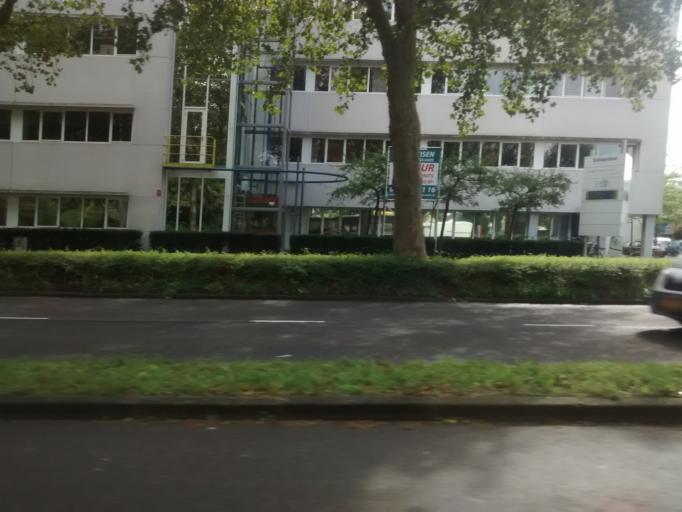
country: NL
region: Utrecht
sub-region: Gemeente Utrecht
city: Lunetten
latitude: 52.0666
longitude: 5.1169
